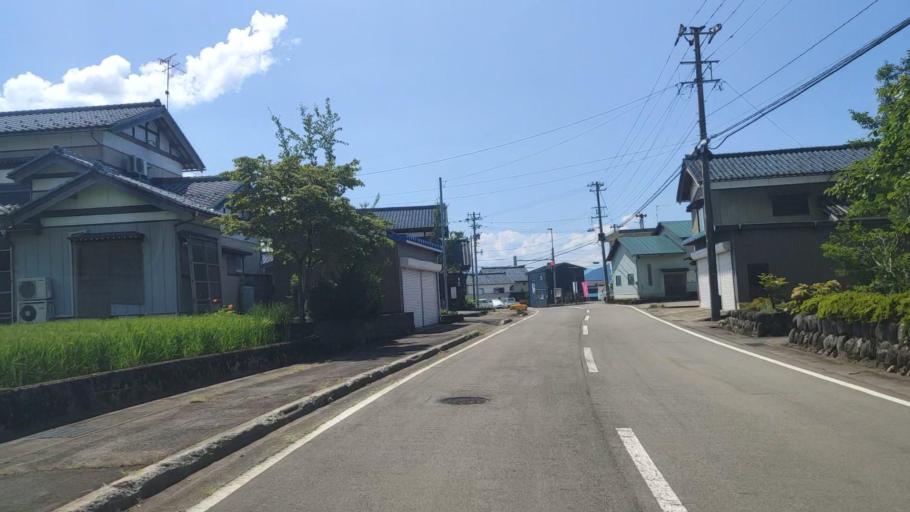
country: JP
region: Fukui
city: Katsuyama
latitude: 36.0908
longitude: 136.4913
